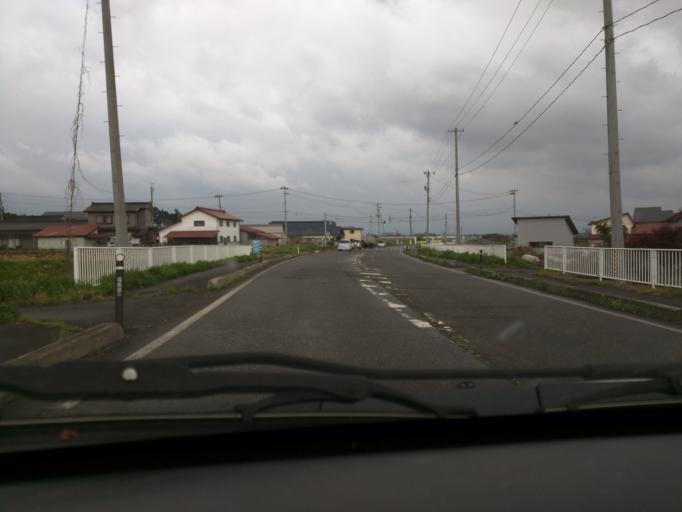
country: JP
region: Fukushima
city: Kitakata
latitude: 37.6114
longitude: 139.9125
